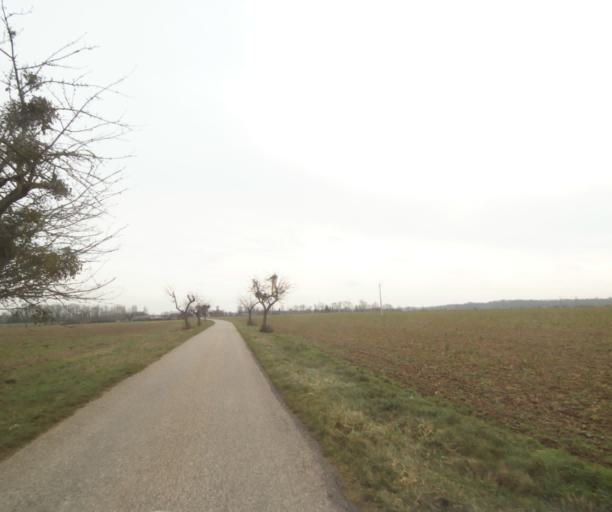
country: FR
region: Champagne-Ardenne
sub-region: Departement de la Haute-Marne
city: Villiers-en-Lieu
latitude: 48.6720
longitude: 4.8841
